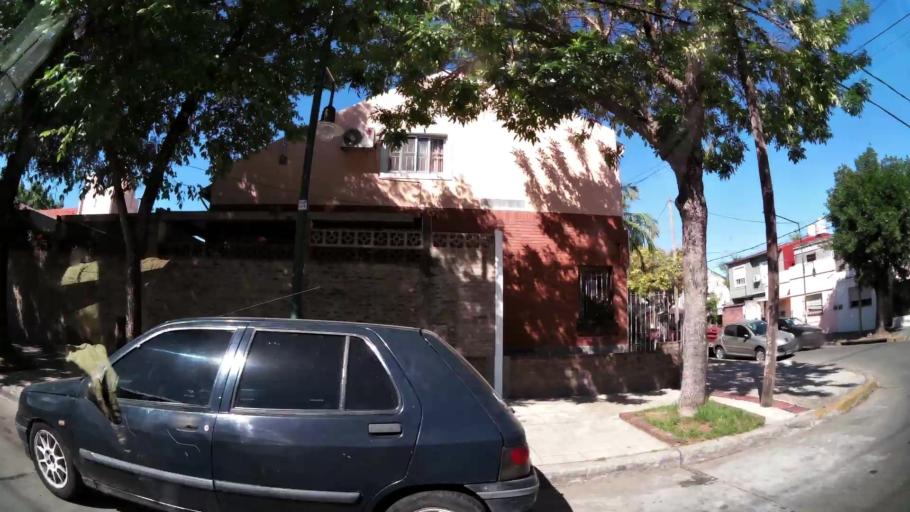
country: AR
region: Buenos Aires
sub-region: Partido de San Isidro
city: San Isidro
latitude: -34.4646
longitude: -58.5410
